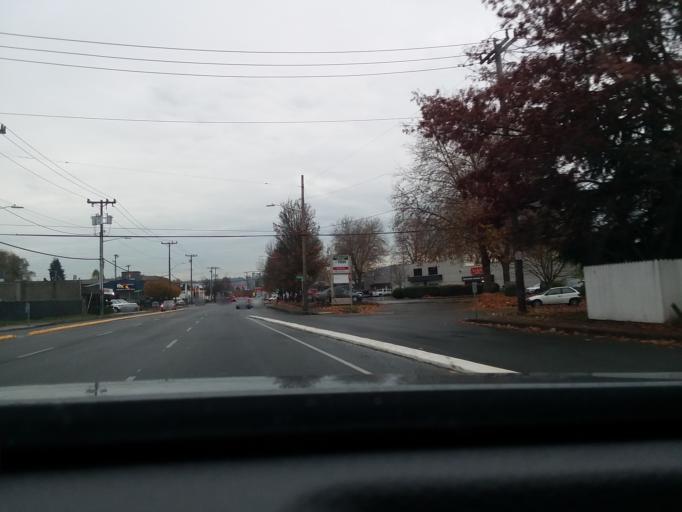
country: US
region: Washington
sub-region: King County
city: White Center
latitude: 47.5499
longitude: -122.3208
